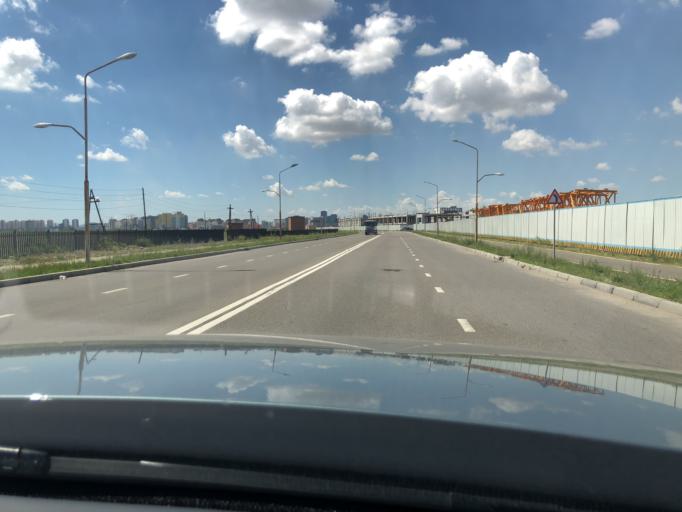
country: MN
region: Ulaanbaatar
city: Ulaanbaatar
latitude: 47.9047
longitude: 106.9744
